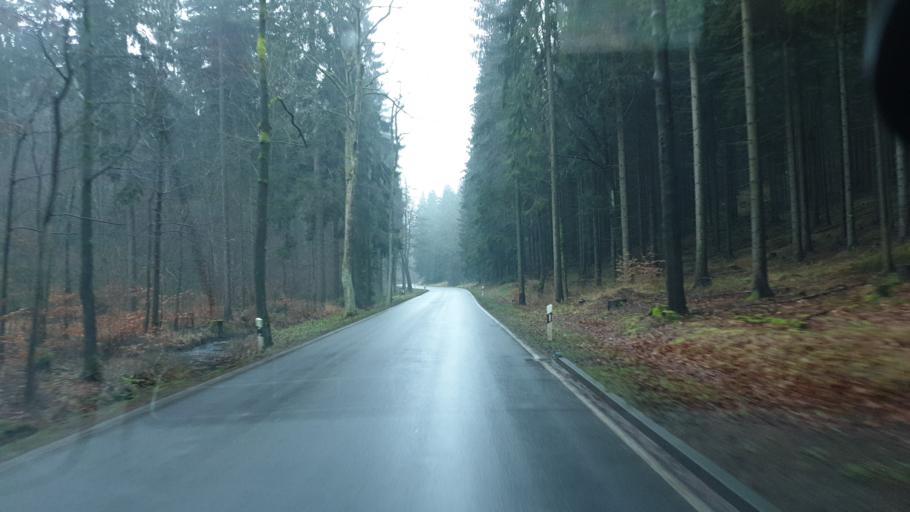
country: DE
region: Saxony
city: Seiffen
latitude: 50.6349
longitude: 13.4217
